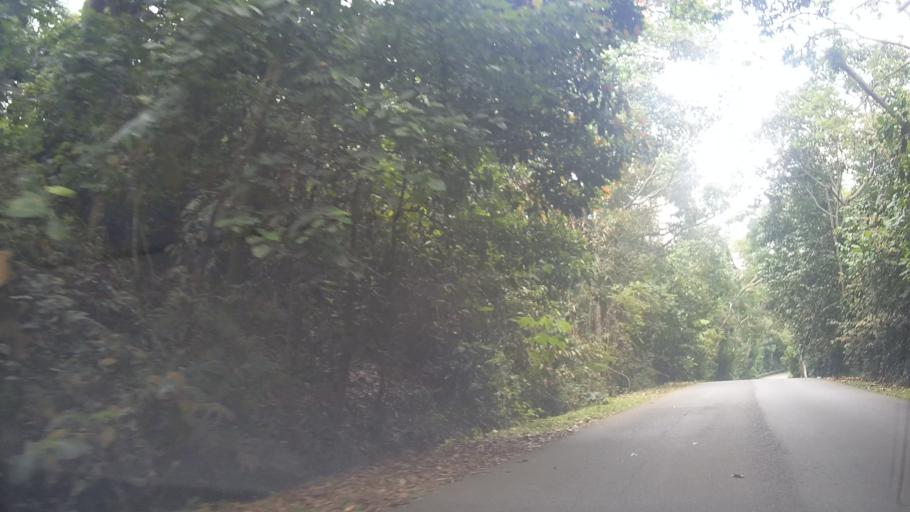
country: SG
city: Singapore
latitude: 1.3539
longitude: 103.7936
